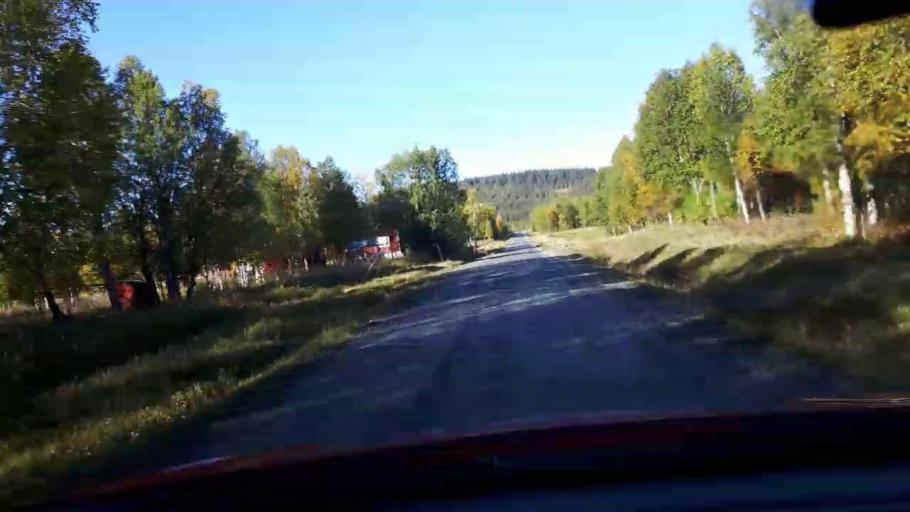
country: NO
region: Nord-Trondelag
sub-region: Lierne
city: Sandvika
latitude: 64.6098
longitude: 13.7498
